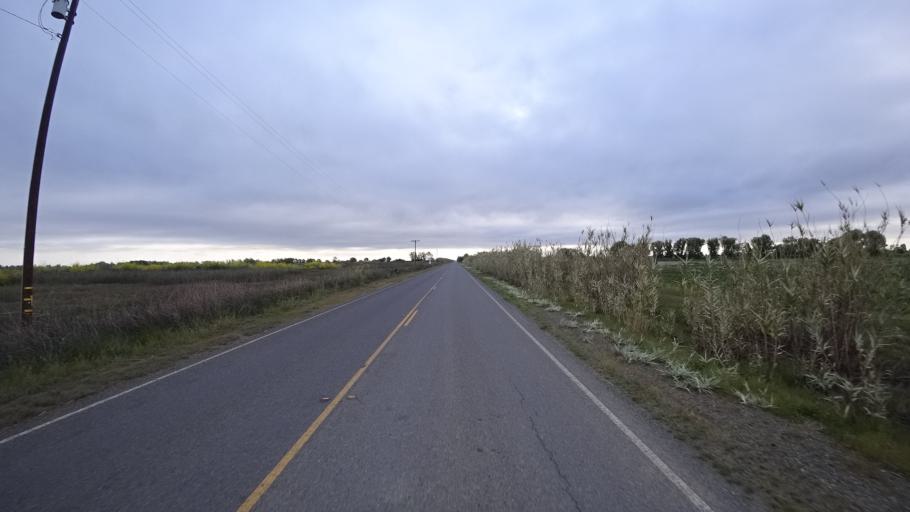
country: US
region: California
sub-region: Glenn County
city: Willows
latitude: 39.4062
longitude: -122.1354
